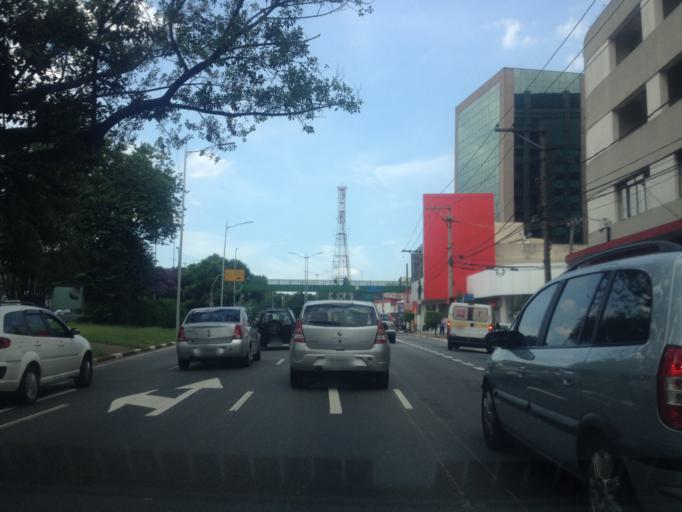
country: BR
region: Sao Paulo
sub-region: Diadema
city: Diadema
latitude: -23.6241
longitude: -46.6618
